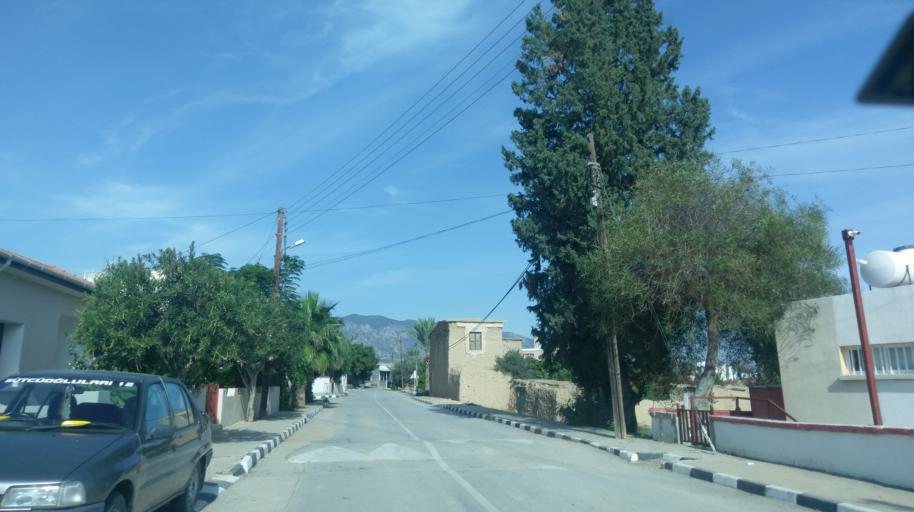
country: CY
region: Ammochostos
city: Lefkonoiko
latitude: 35.2532
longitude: 33.6030
